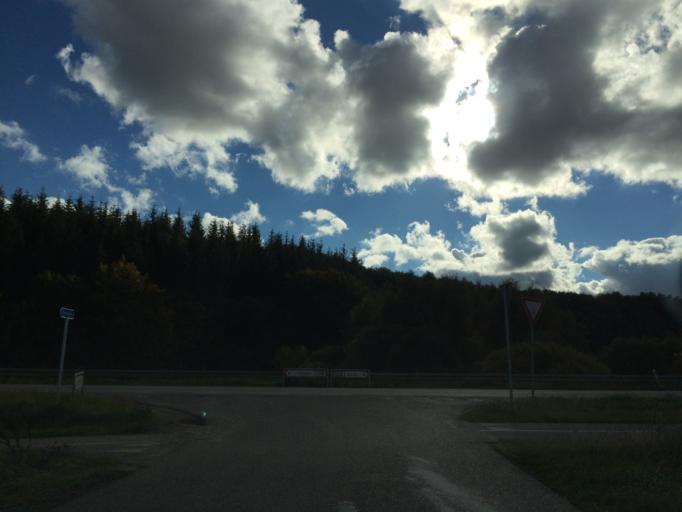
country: DK
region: Central Jutland
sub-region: Skanderborg Kommune
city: Ry
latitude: 56.1531
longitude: 9.7547
